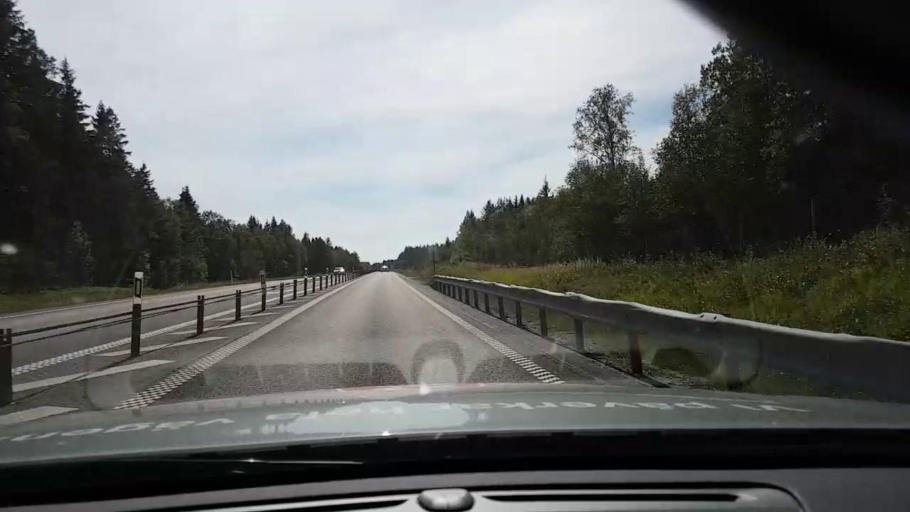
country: SE
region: Vaesternorrland
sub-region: OErnskoeldsviks Kommun
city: Husum
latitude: 63.4011
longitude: 19.2010
